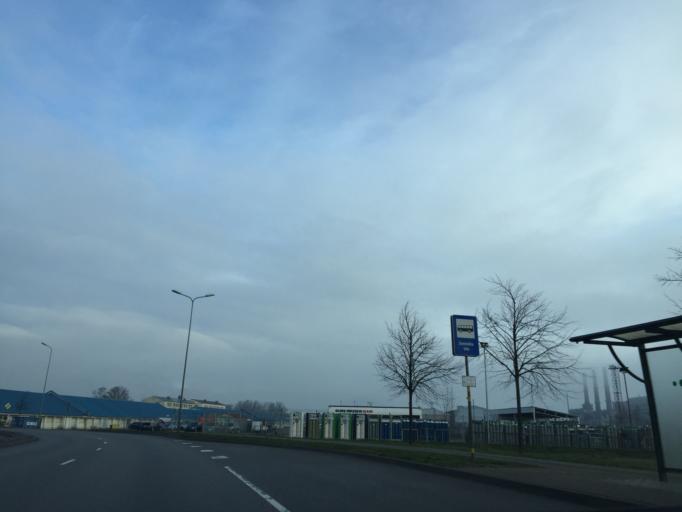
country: LV
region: Liepaja
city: Liepaja
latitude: 56.5206
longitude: 21.0279
